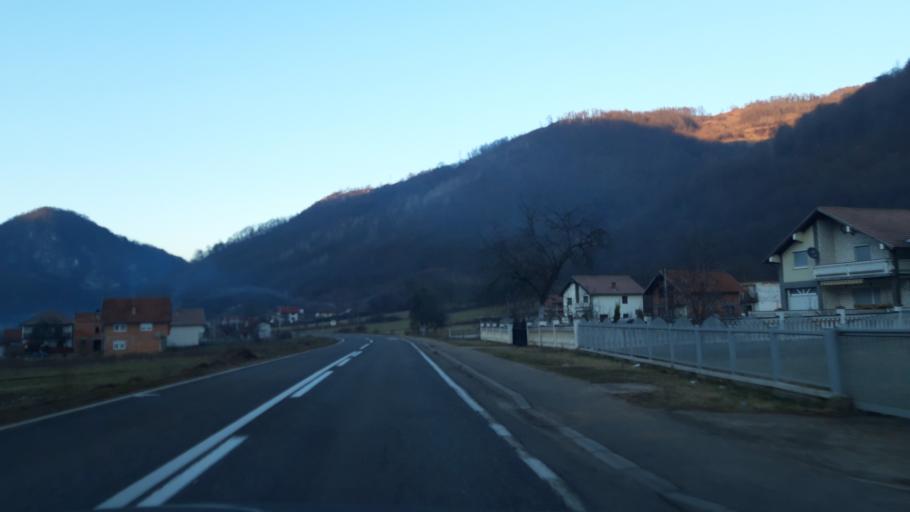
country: BA
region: Republika Srpska
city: Milici
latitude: 44.2541
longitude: 19.1080
